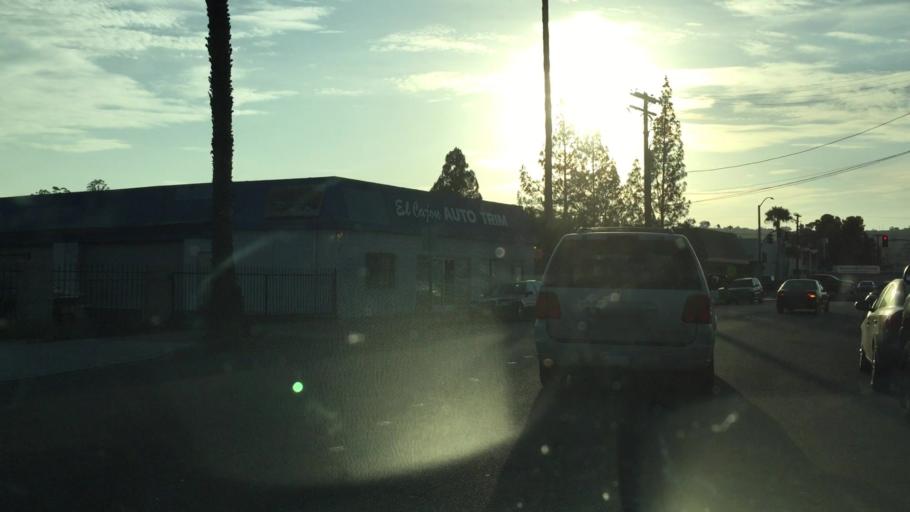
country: US
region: California
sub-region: San Diego County
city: El Cajon
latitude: 32.7924
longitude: -116.9689
